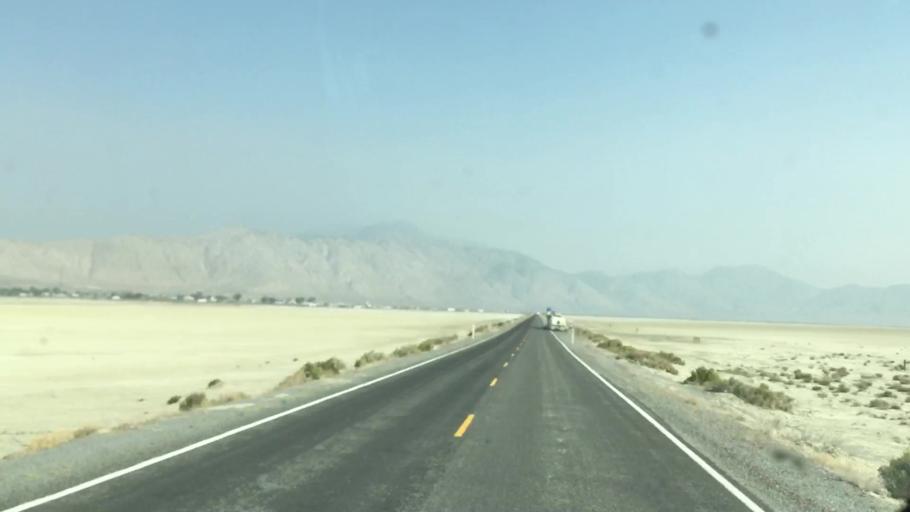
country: US
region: Nevada
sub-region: Pershing County
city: Lovelock
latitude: 40.6367
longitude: -119.3398
